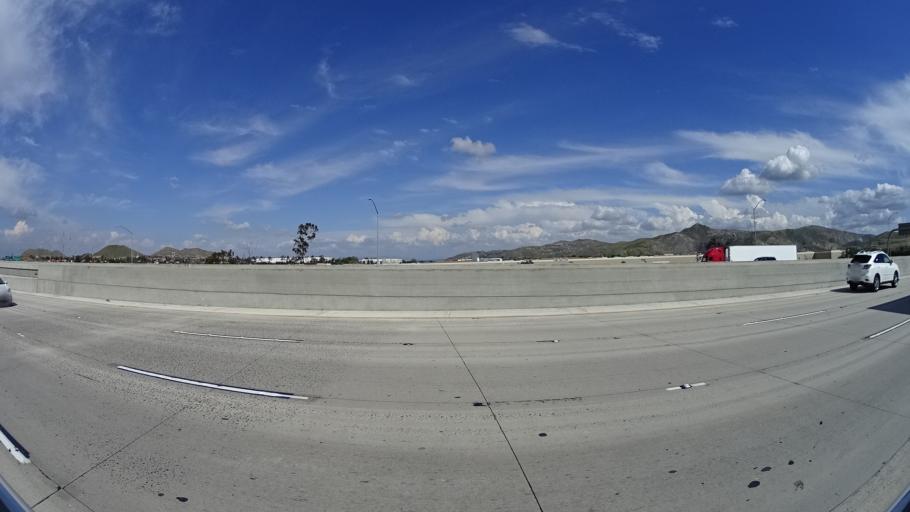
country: US
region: California
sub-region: Riverside County
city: Corona
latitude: 33.8764
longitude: -117.5459
